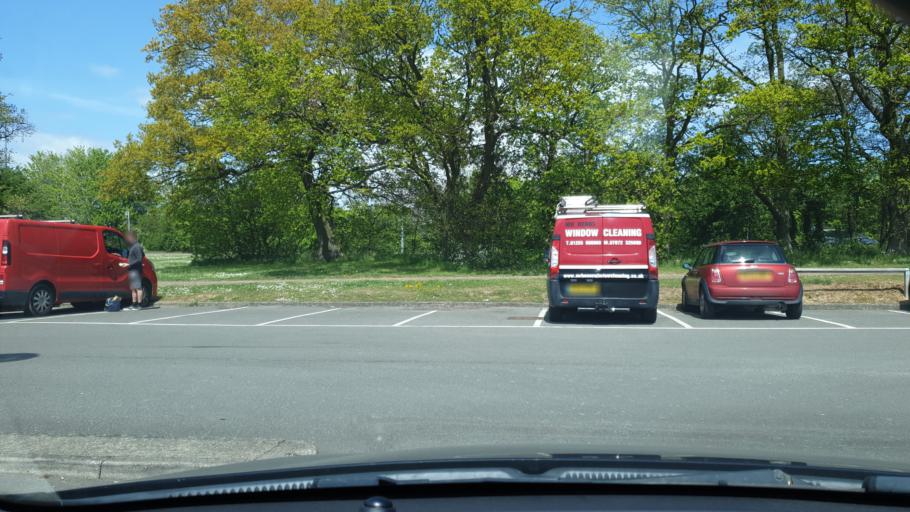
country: GB
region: England
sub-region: Essex
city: Little Clacton
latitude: 51.8177
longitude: 1.1494
